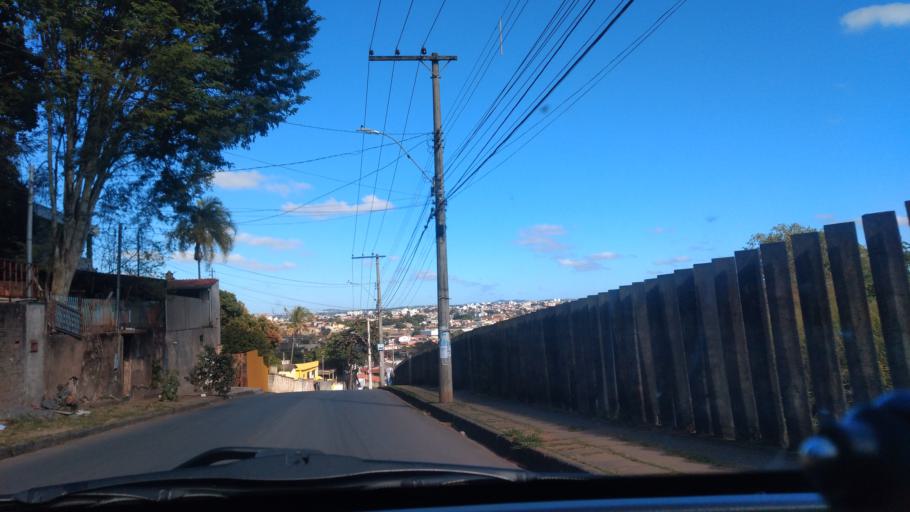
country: BR
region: Minas Gerais
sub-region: Santa Luzia
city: Santa Luzia
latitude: -19.8099
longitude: -43.9408
